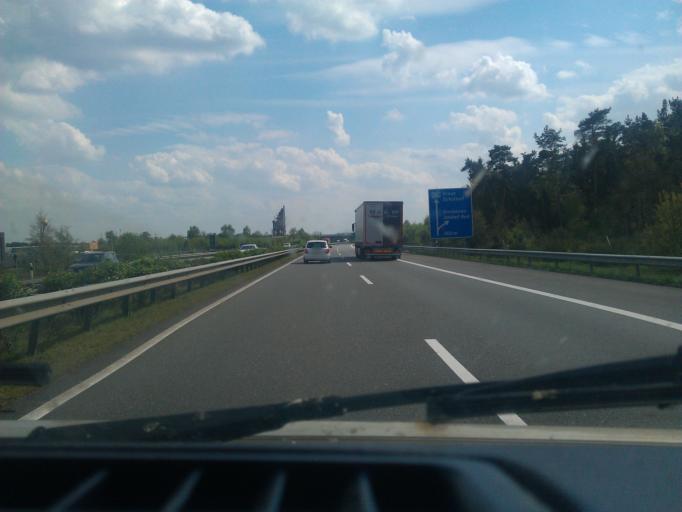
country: DE
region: Lower Saxony
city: Schuttorf
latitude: 52.3632
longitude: 7.2556
